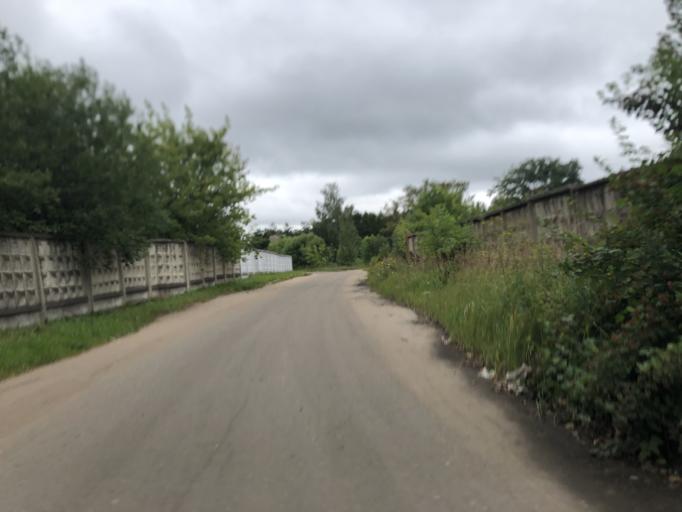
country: RU
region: Tverskaya
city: Rzhev
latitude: 56.2404
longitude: 34.3318
